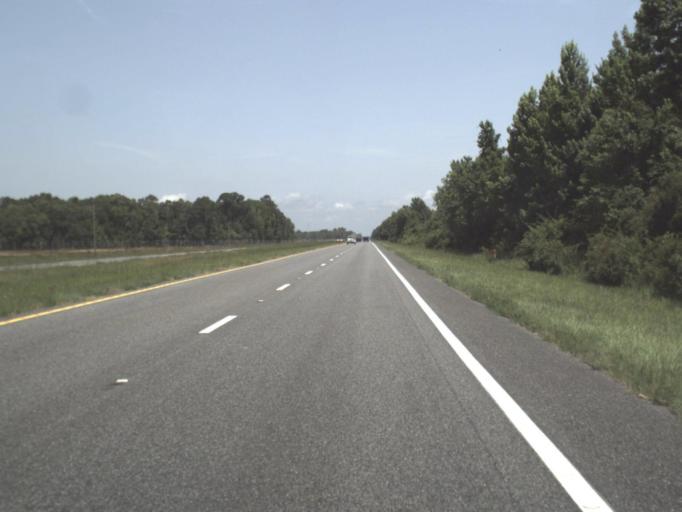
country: US
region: Florida
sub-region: Taylor County
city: Steinhatchee
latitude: 29.8181
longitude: -83.3497
